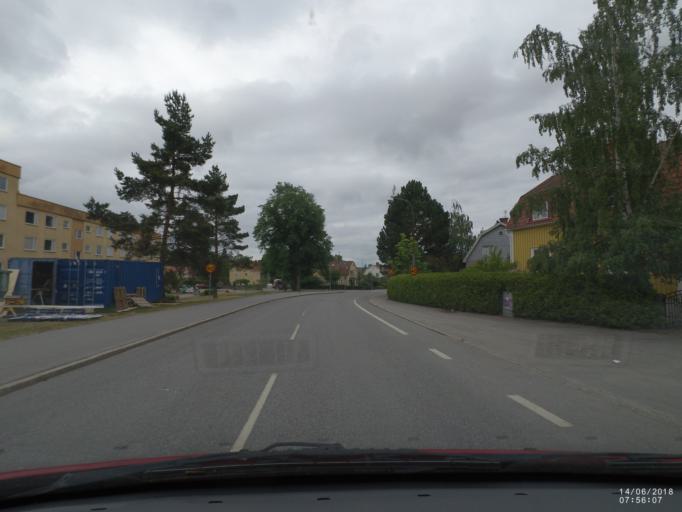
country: SE
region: Soedermanland
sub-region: Nykopings Kommun
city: Nykoping
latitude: 58.7598
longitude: 17.0218
